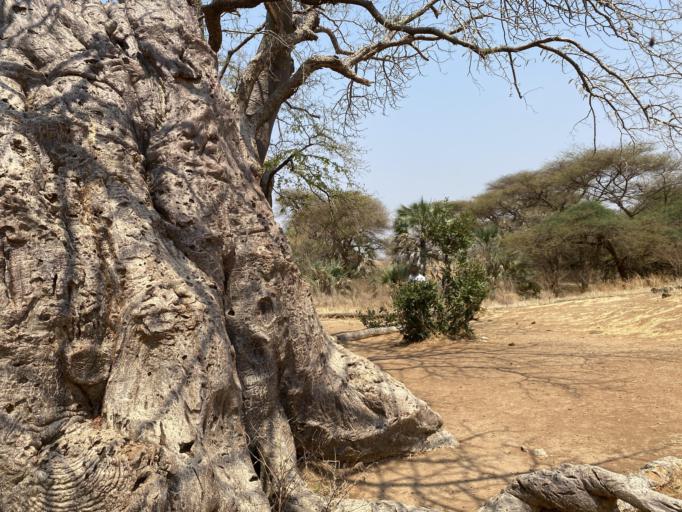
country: ZW
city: Chirundu
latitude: -16.1604
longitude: 28.8021
